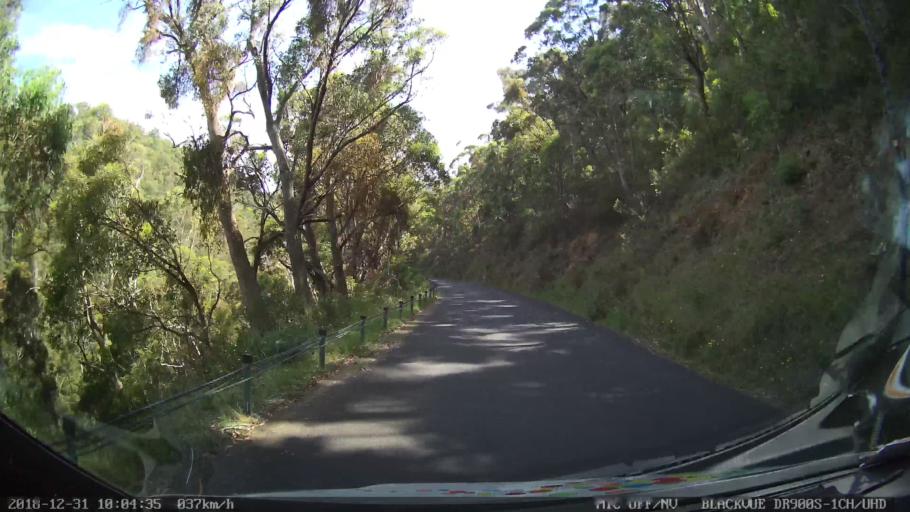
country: AU
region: New South Wales
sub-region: Snowy River
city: Jindabyne
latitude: -36.5308
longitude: 148.1921
